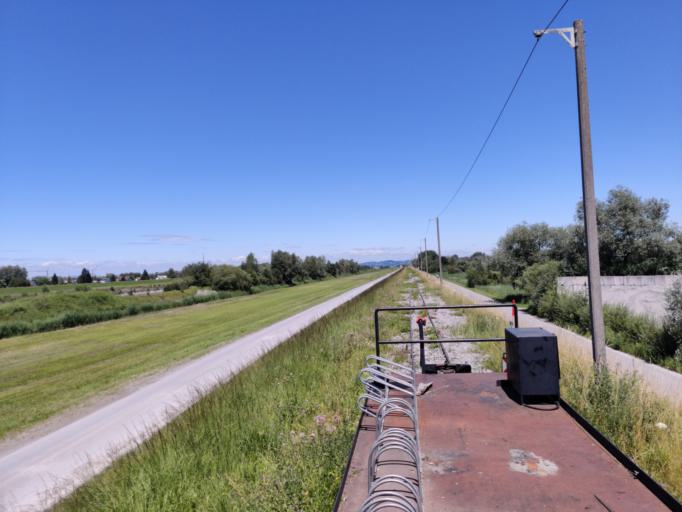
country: AT
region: Vorarlberg
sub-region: Politischer Bezirk Bregenz
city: Fussach
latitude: 47.4793
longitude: 9.6713
